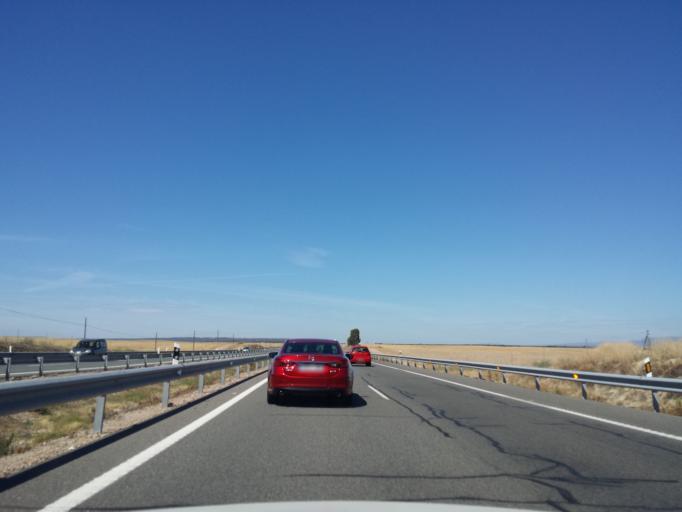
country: ES
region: Extremadura
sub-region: Provincia de Caceres
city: Berrocalejo
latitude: 39.8924
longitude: -5.3828
